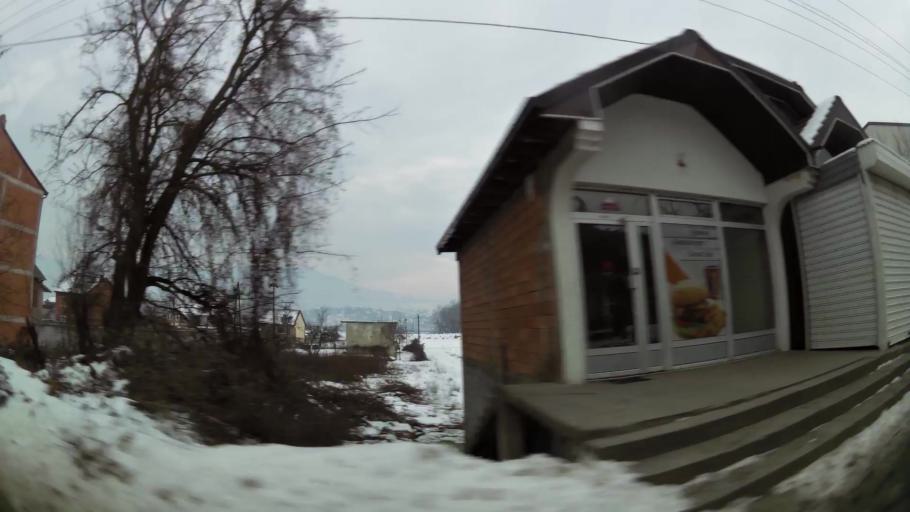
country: MK
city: Kondovo
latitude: 42.0115
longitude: 21.3080
